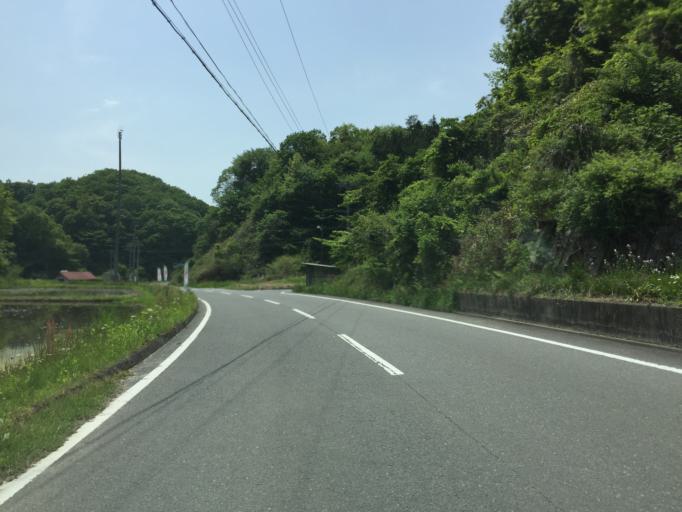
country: JP
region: Fukushima
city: Ishikawa
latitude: 37.1854
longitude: 140.5229
